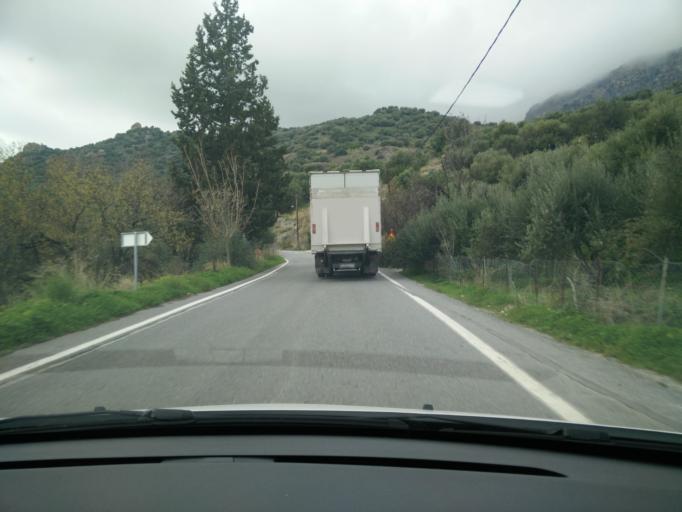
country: GR
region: Crete
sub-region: Nomos Lasithiou
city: Gra Liyia
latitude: 35.0256
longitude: 25.5644
